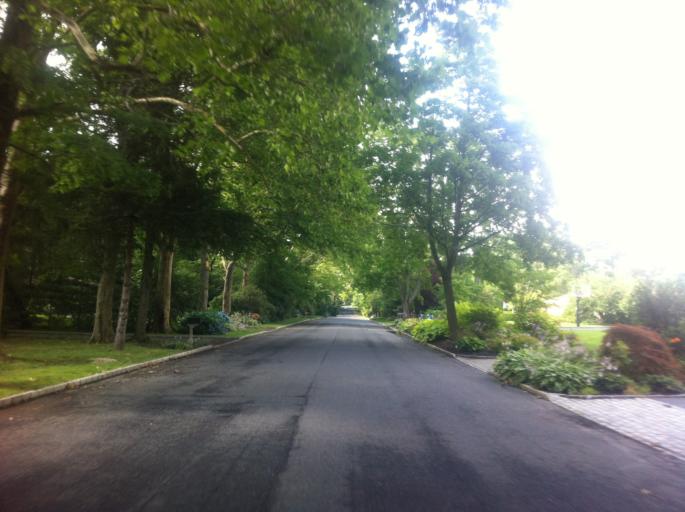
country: US
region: New York
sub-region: Nassau County
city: Old Brookville
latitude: 40.8492
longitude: -73.6069
